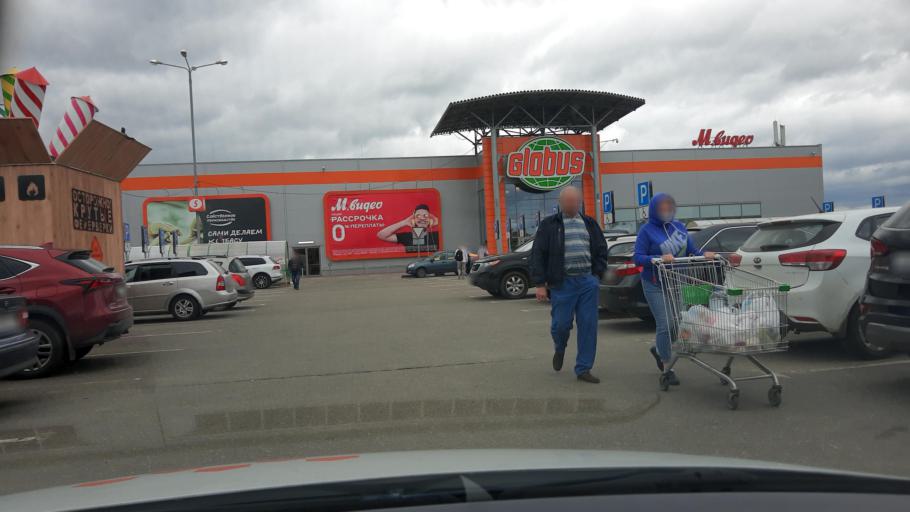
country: RU
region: Moskovskaya
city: Elektrostal'
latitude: 55.7603
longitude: 38.4346
